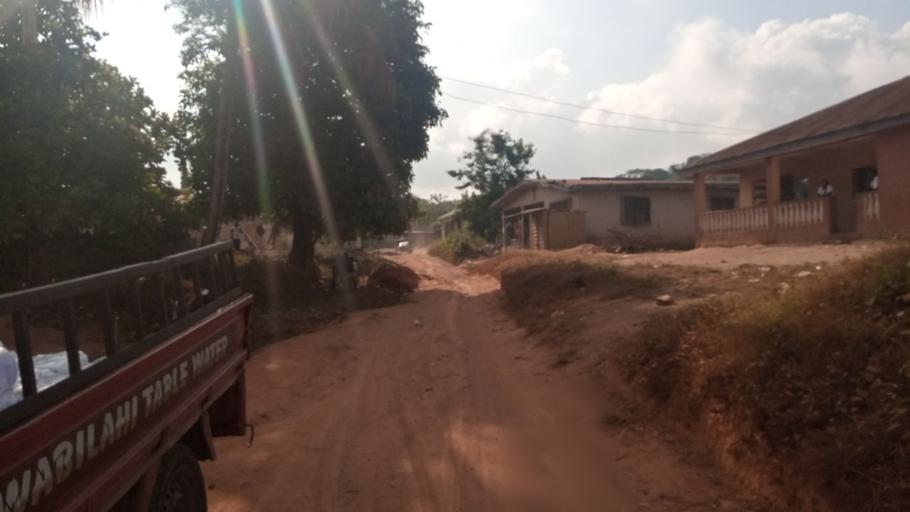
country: NG
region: Osun
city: Iragbiji
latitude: 7.9344
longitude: 4.7130
